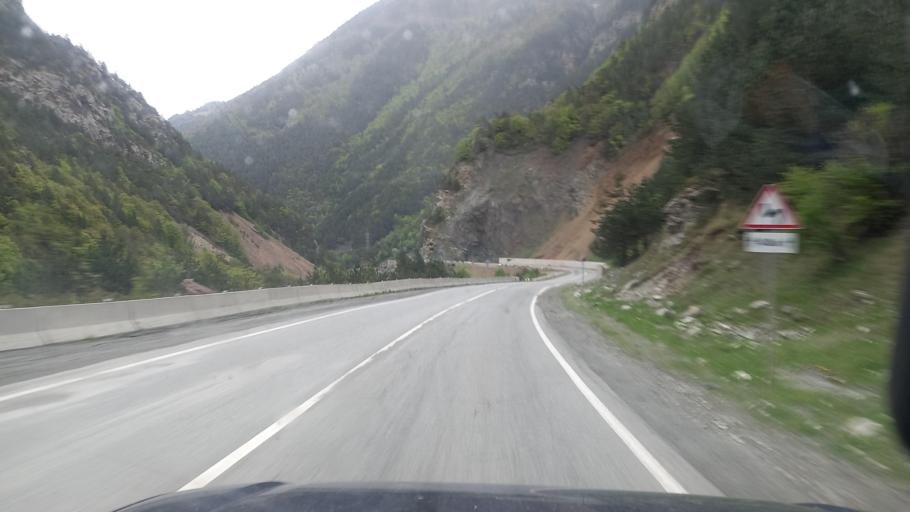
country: RU
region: North Ossetia
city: Mizur
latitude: 42.8072
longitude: 44.0165
